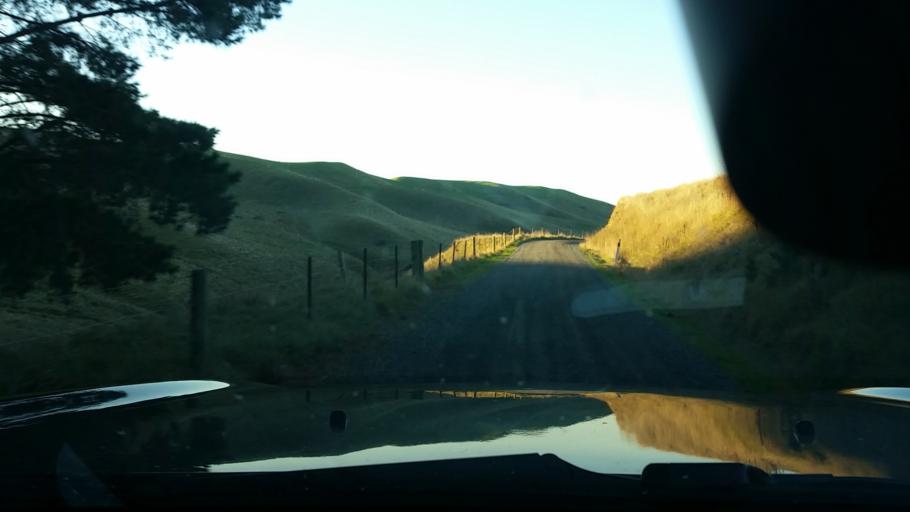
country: NZ
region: Marlborough
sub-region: Marlborough District
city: Blenheim
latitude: -41.7500
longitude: 174.0600
